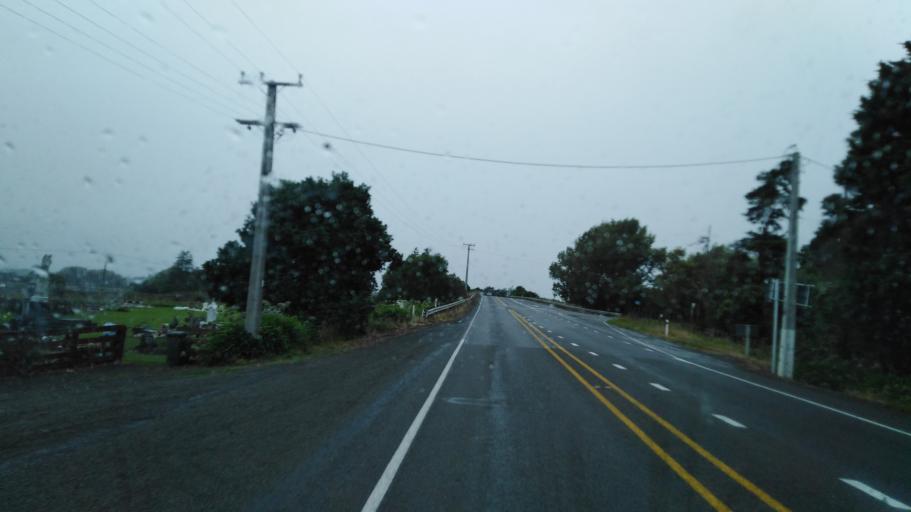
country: NZ
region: Manawatu-Wanganui
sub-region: Horowhenua District
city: Levin
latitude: -40.6747
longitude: 175.2403
